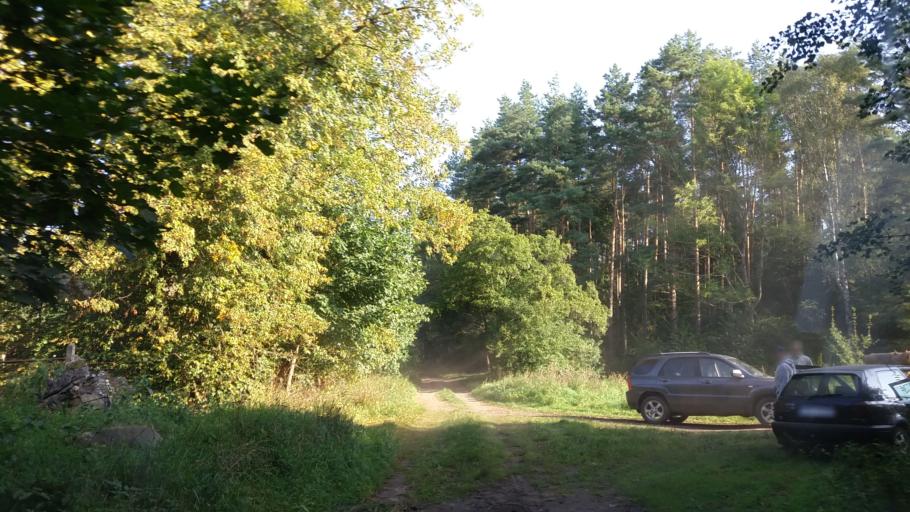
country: PL
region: West Pomeranian Voivodeship
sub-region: Powiat choszczenski
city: Recz
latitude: 53.1969
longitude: 15.5423
